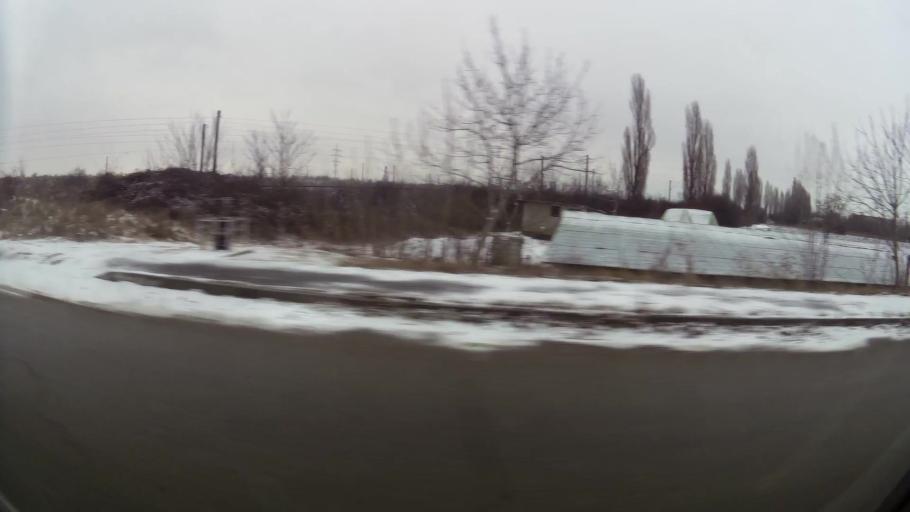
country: RO
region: Prahova
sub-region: Comuna Berceni
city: Corlatesti
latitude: 44.9316
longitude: 26.0617
